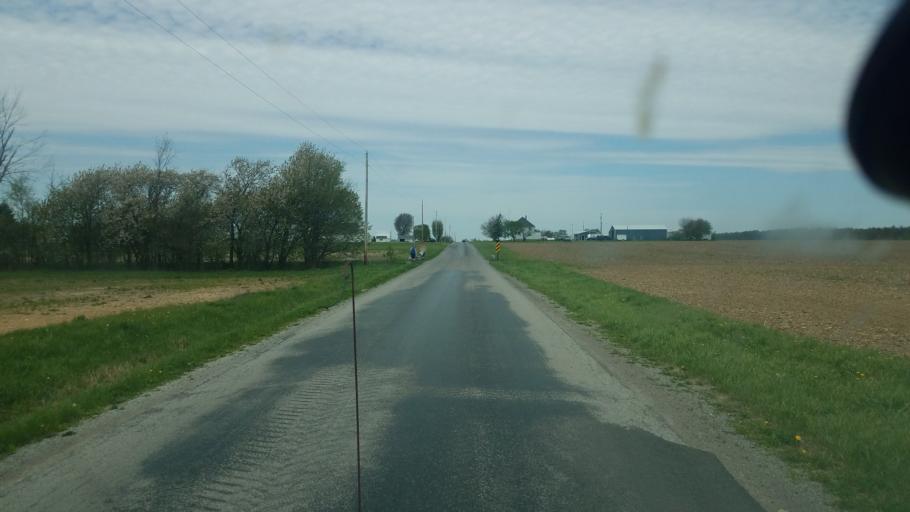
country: US
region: Ohio
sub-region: Hardin County
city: Ada
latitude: 40.8141
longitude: -83.8800
